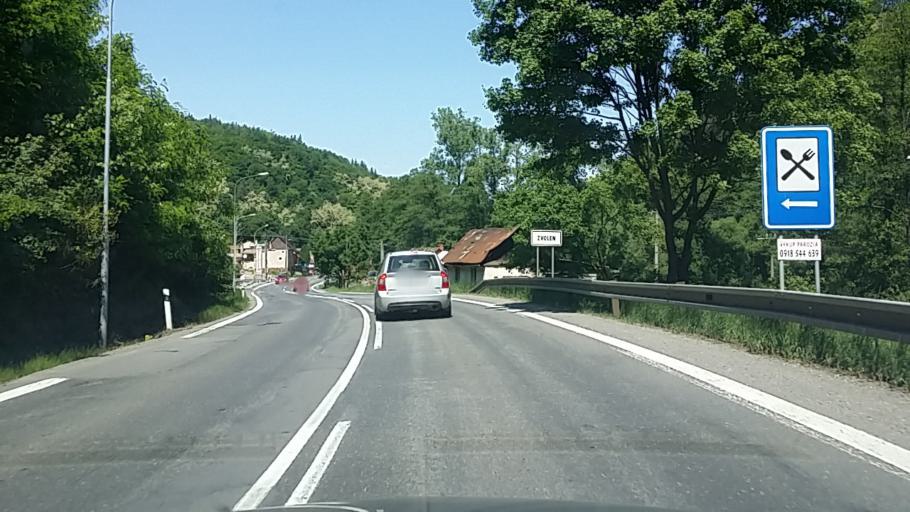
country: SK
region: Banskobystricky
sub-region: Okres Banska Bystrica
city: Zvolen
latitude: 48.5568
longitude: 19.1329
